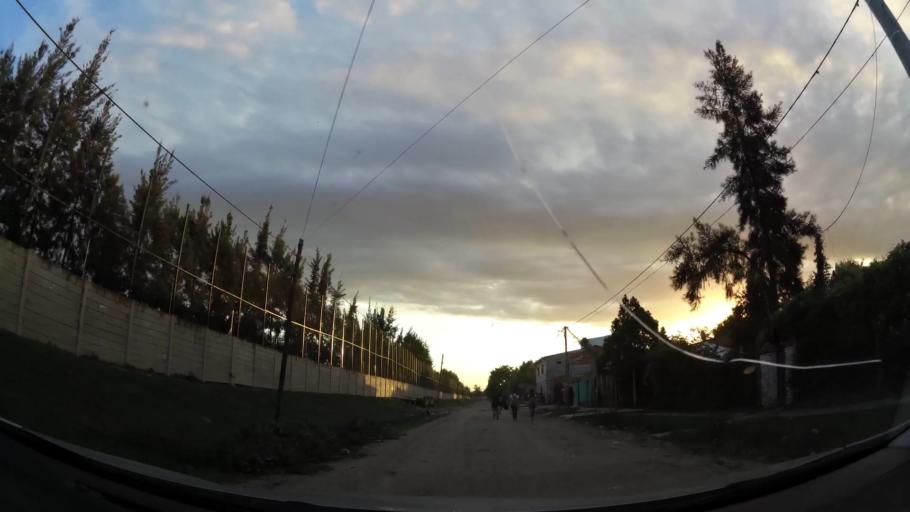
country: AR
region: Buenos Aires
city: Santa Catalina - Dique Lujan
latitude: -34.4348
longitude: -58.6639
